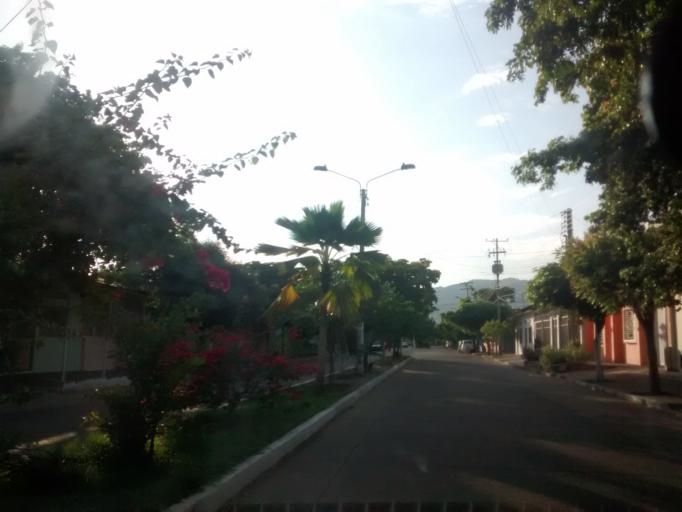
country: CO
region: Tolima
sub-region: Flandes
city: Flandes
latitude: 4.2925
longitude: -74.8189
